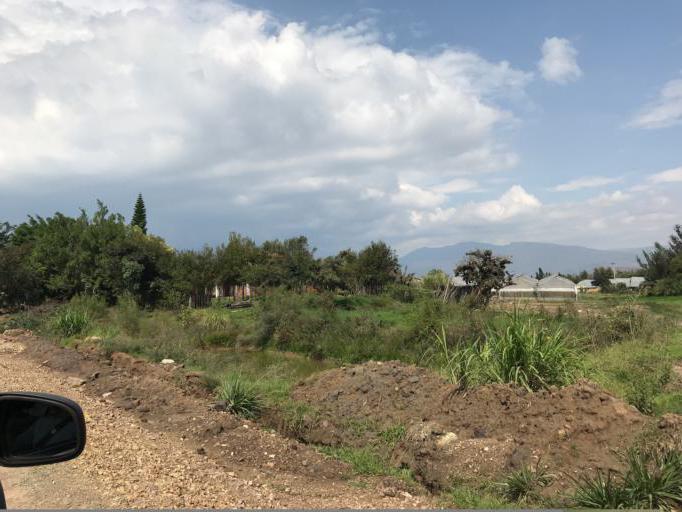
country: CO
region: Boyaca
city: Sutamarchan
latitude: 5.6277
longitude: -73.6125
